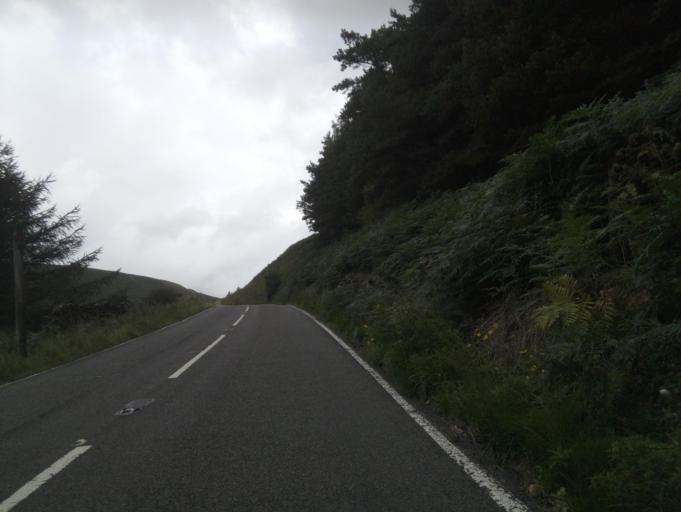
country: GB
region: England
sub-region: Kirklees
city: Meltham
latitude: 53.5065
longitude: -1.8525
